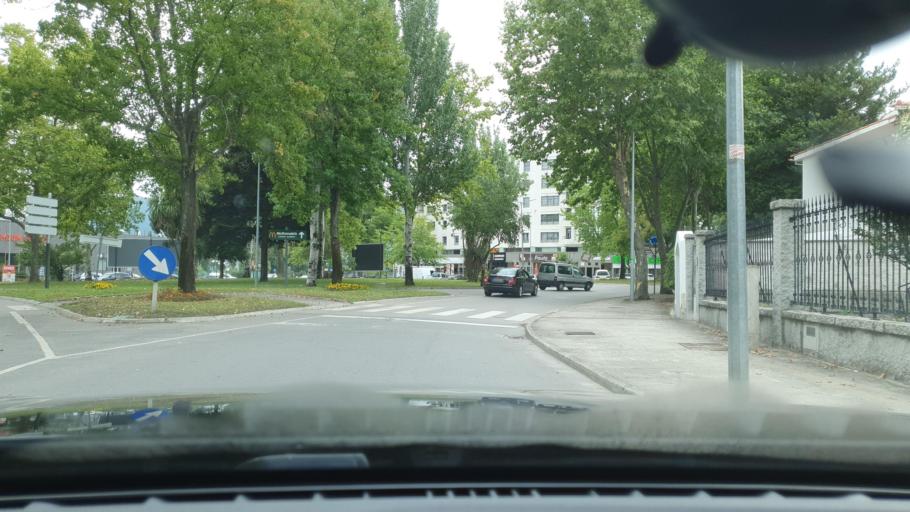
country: PT
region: Vila Real
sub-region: Chaves
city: Chaves
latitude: 41.7386
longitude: -7.4752
